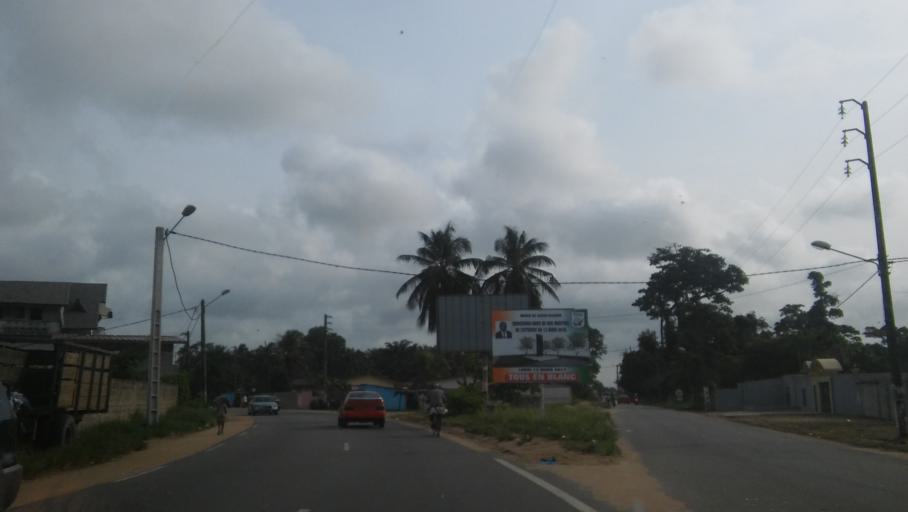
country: CI
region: Sud-Comoe
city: Grand-Bassam
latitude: 5.2164
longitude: -3.7295
